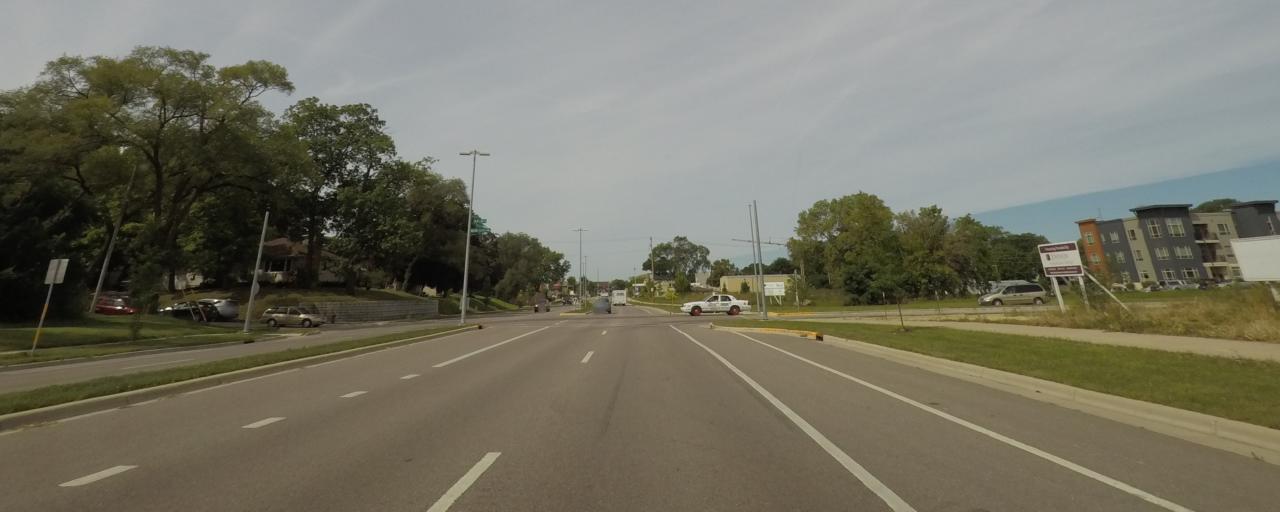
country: US
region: Wisconsin
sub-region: Dane County
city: Monona
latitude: 43.0840
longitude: -89.3185
